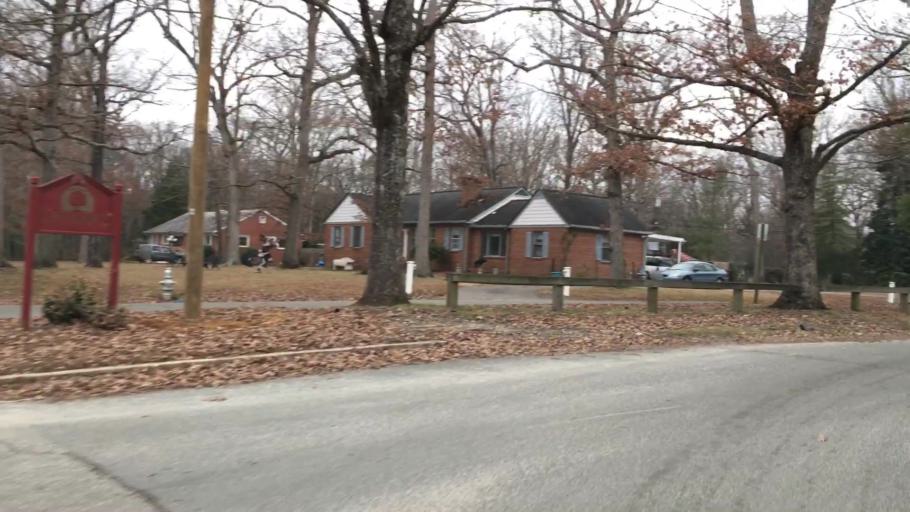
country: US
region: Virginia
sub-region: Chesterfield County
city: Bon Air
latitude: 37.5335
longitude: -77.5736
